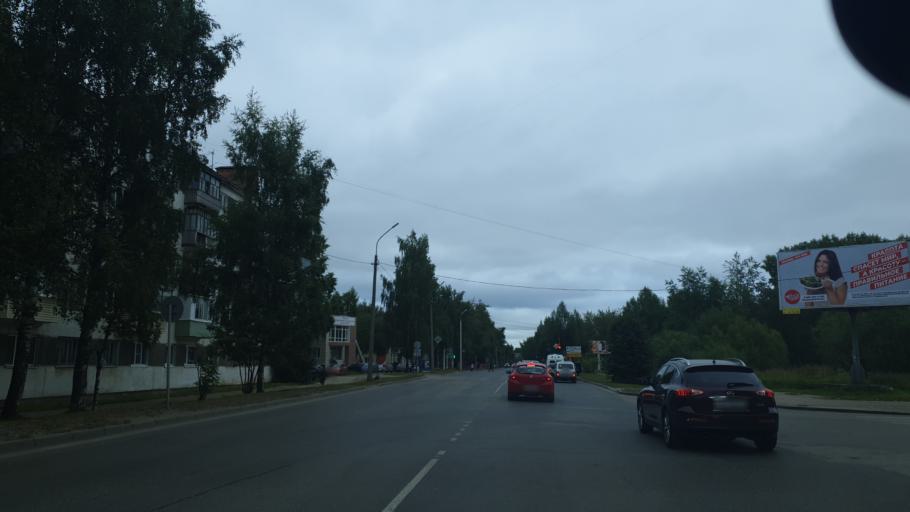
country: RU
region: Komi Republic
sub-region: Syktyvdinskiy Rayon
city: Syktyvkar
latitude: 61.6566
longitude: 50.8055
